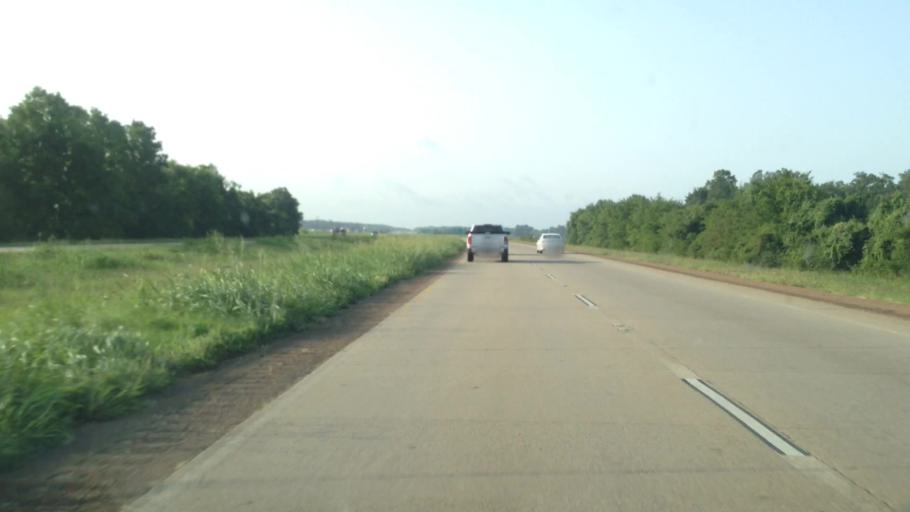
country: US
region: Louisiana
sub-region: Rapides Parish
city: Woodworth
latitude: 31.1870
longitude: -92.4722
